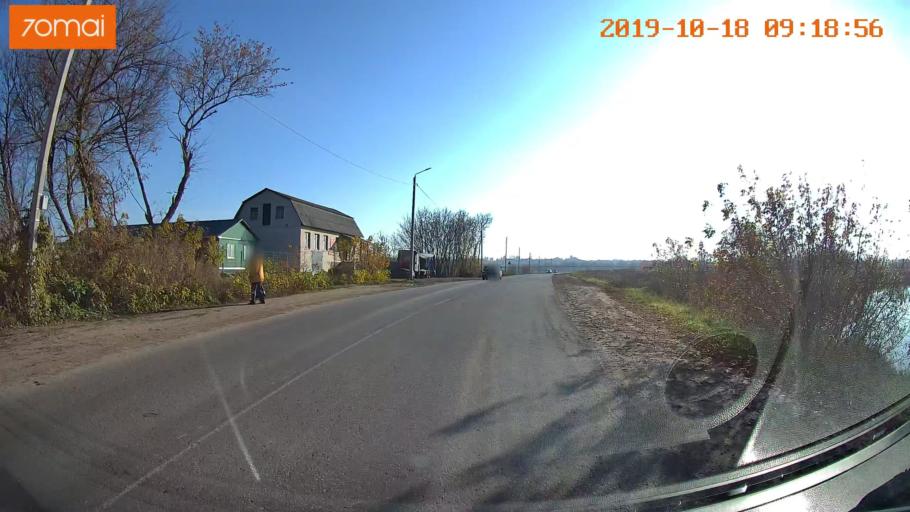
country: RU
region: Tula
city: Yefremov
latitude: 53.1351
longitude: 38.1237
